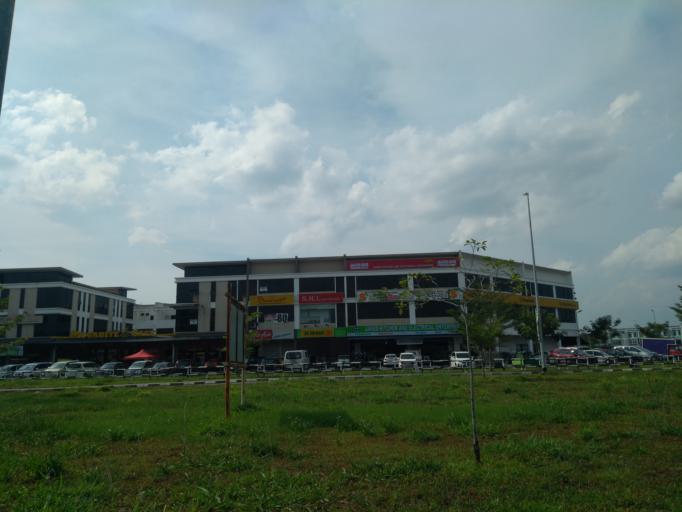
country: MY
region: Sarawak
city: Kuching
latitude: 1.5727
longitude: 110.3033
